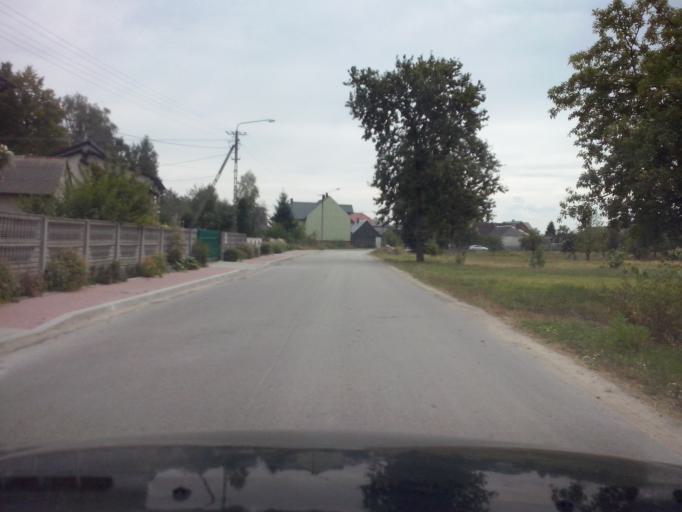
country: PL
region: Swietokrzyskie
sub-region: Powiat kielecki
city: Lagow
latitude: 50.7401
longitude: 21.0687
